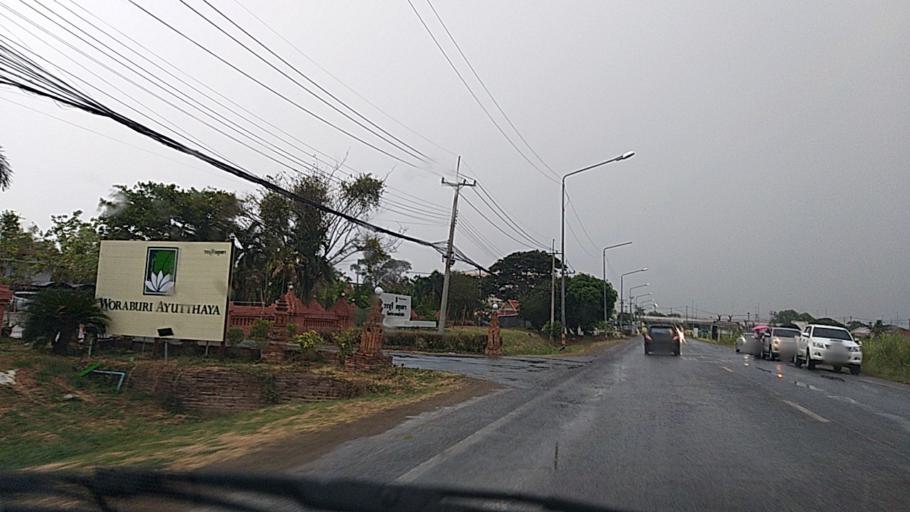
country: TH
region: Phra Nakhon Si Ayutthaya
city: Phra Nakhon Si Ayutthaya
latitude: 14.3489
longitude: 100.5842
